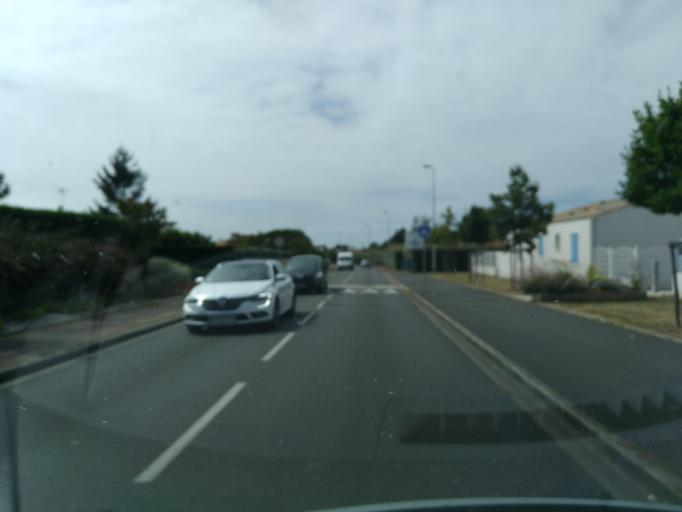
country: FR
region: Poitou-Charentes
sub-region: Departement de la Charente-Maritime
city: Saint-Palais-sur-Mer
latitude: 45.6532
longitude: -1.0844
